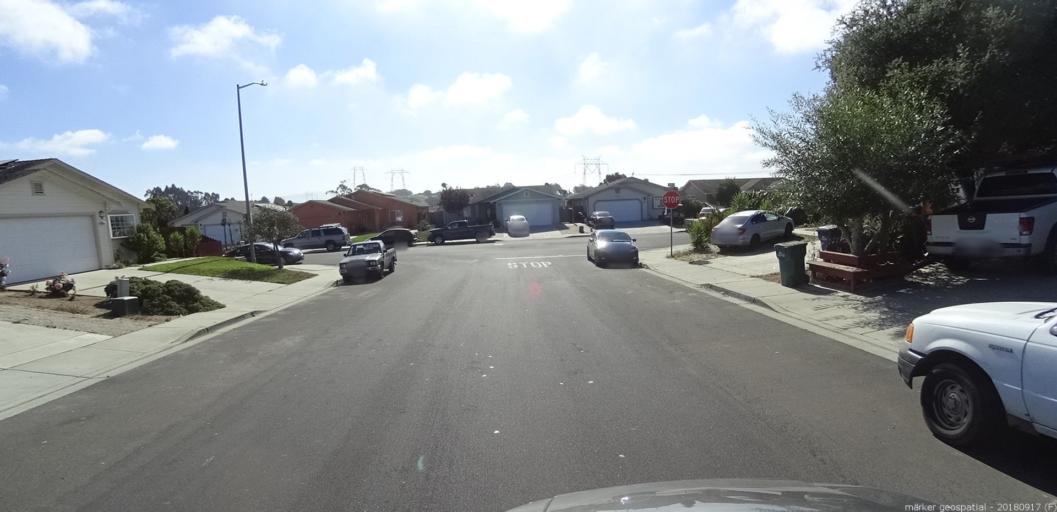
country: US
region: California
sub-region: Monterey County
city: Castroville
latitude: 36.7858
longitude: -121.7276
